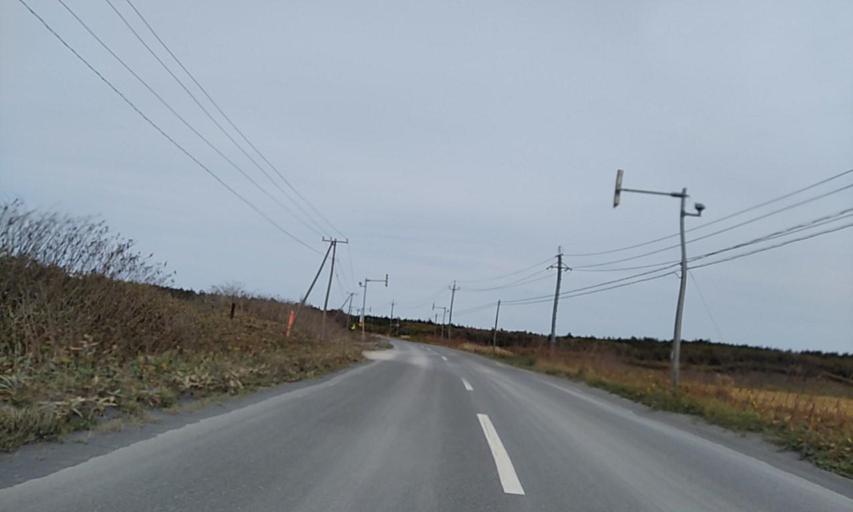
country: JP
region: Hokkaido
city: Makubetsu
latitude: 44.9952
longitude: 141.6912
